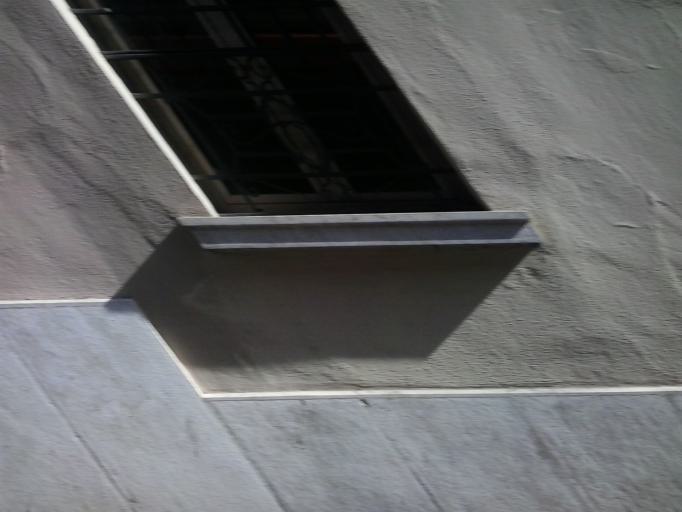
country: IT
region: Lombardy
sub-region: Provincia di Brescia
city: Brescia
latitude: 45.5345
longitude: 10.2215
